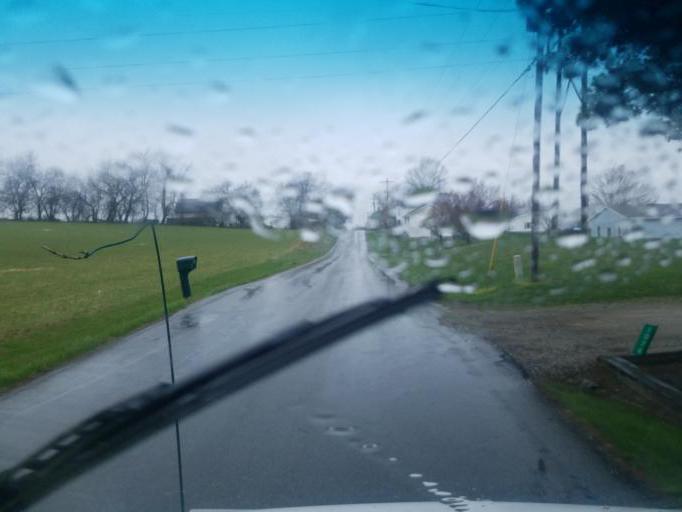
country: US
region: Ohio
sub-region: Wayne County
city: Wooster
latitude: 40.7337
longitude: -81.9331
